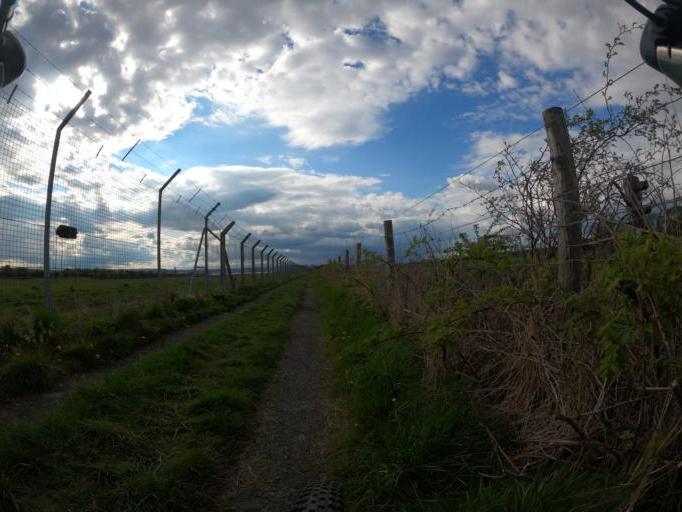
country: GB
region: Scotland
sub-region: Edinburgh
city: Currie
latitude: 55.9428
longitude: -3.3267
